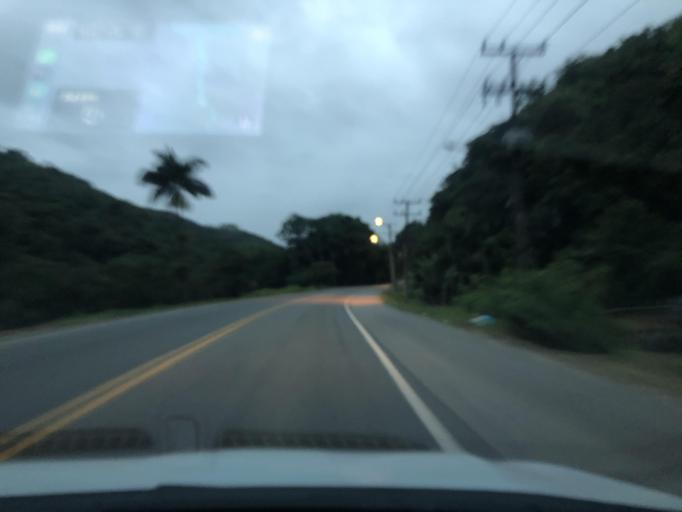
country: BR
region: Santa Catarina
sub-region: Pomerode
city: Pomerode
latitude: -26.7155
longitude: -49.0579
